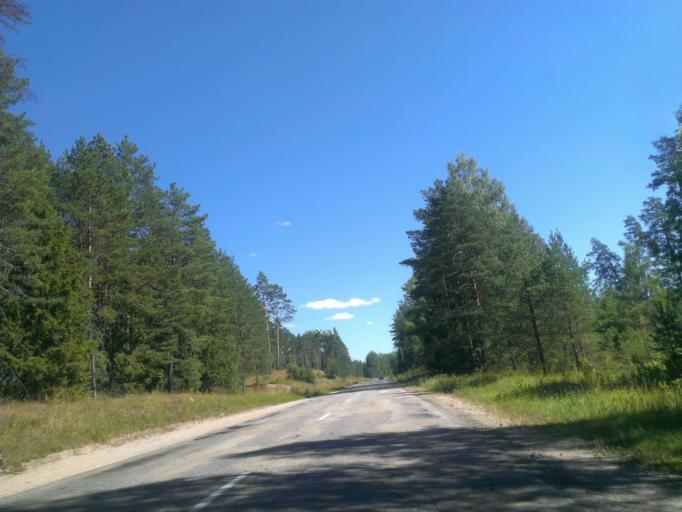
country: LV
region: Incukalns
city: Incukalns
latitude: 57.0296
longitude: 24.7249
